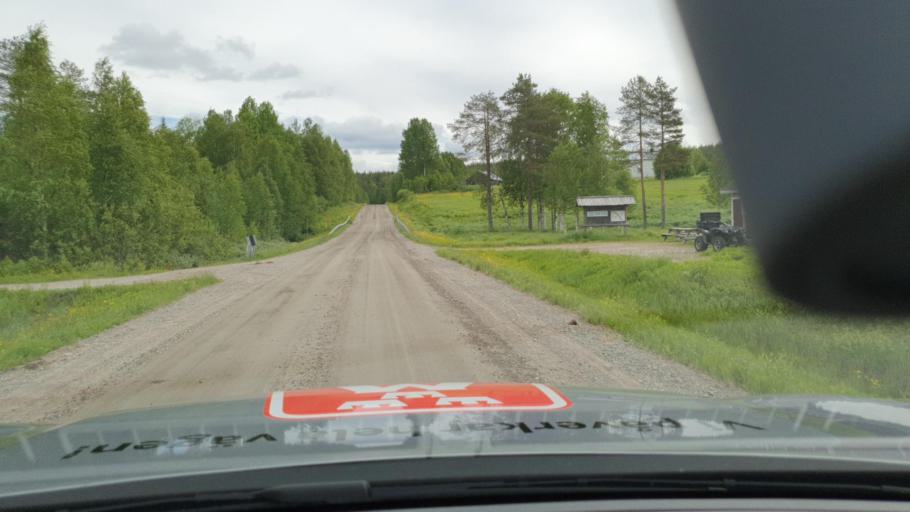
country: SE
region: Norrbotten
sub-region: Kalix Kommun
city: Kalix
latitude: 65.9418
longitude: 23.5349
